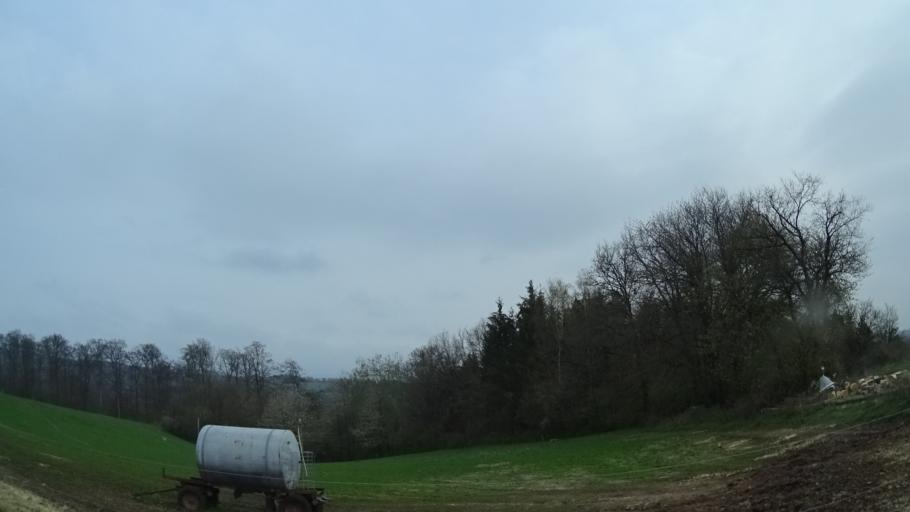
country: DE
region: Rheinland-Pfalz
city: Rimsberg
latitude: 49.6586
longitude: 7.2355
